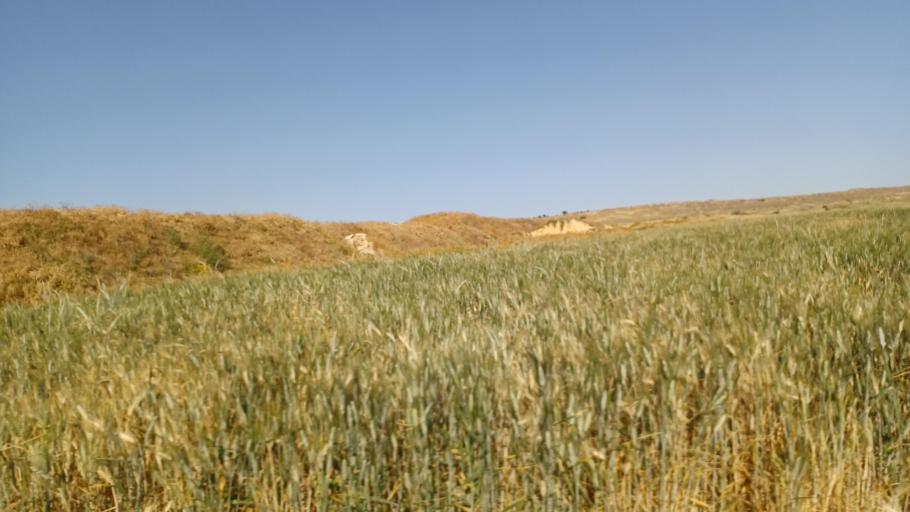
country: CY
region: Lefkosia
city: Mammari
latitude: 35.1582
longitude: 33.2433
